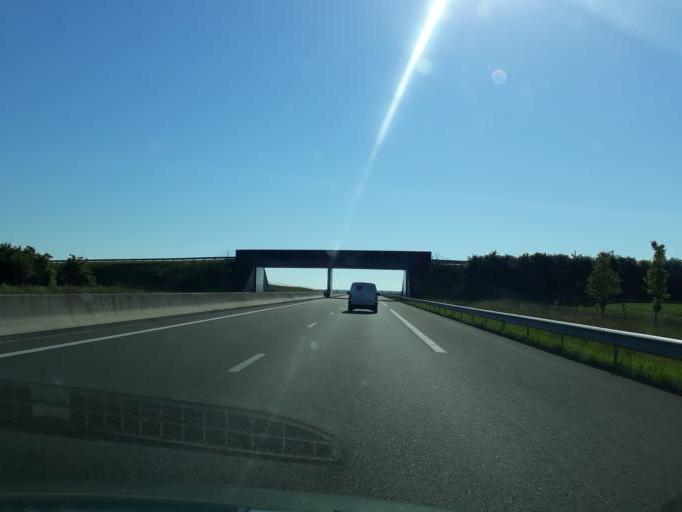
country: FR
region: Centre
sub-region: Departement du Loiret
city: Chevilly
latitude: 48.0486
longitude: 1.9128
